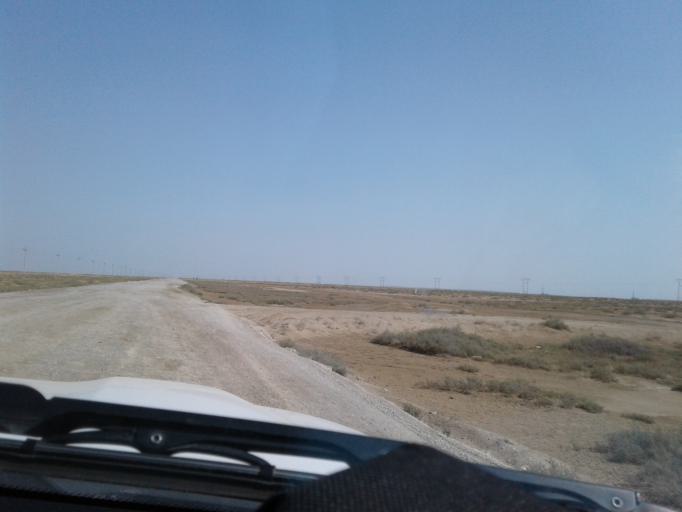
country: IR
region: Golestan
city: Gomishan
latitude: 37.7821
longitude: 53.9165
